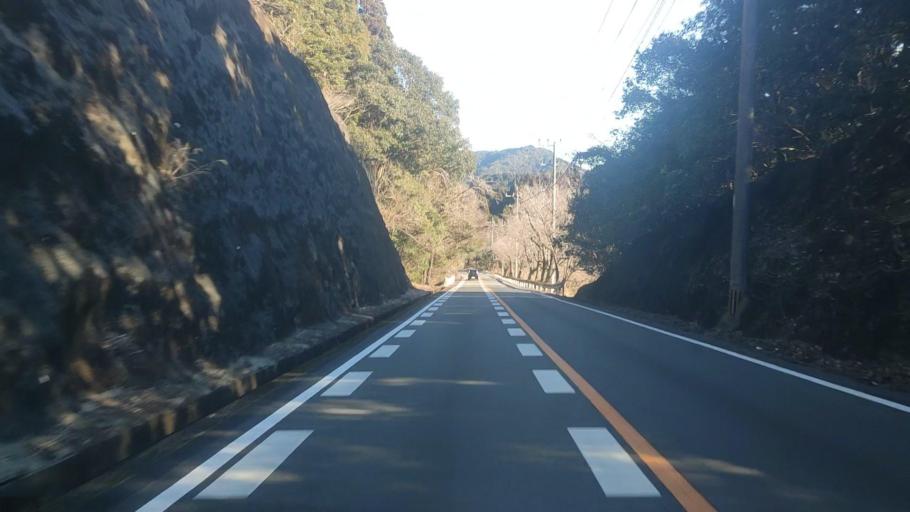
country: JP
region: Miyazaki
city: Nobeoka
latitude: 32.6367
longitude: 131.7414
